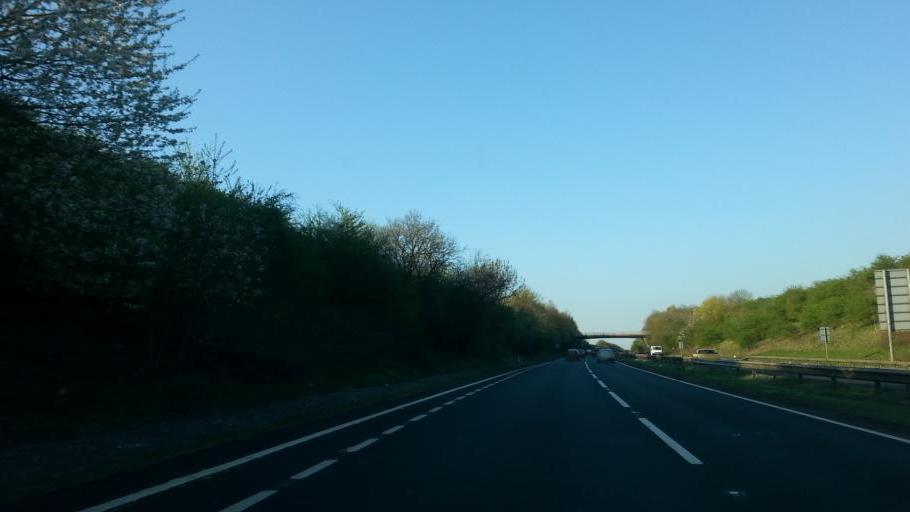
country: GB
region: England
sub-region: Northamptonshire
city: Earls Barton
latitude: 52.2706
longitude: -0.7276
